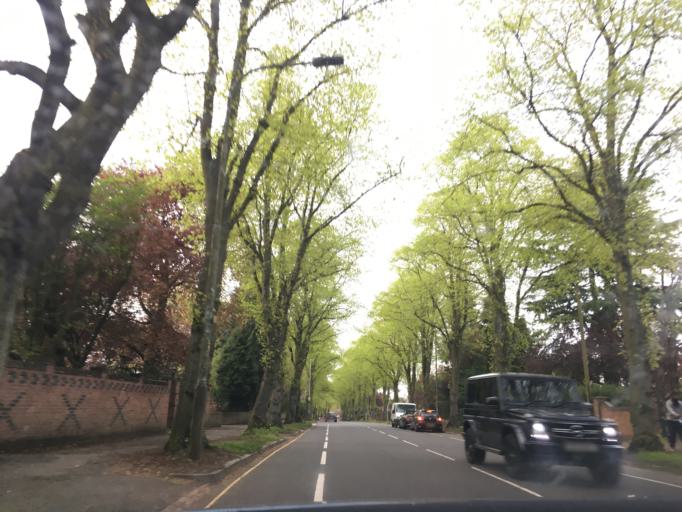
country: GB
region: England
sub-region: Leicestershire
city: Oadby
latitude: 52.6299
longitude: -1.0648
